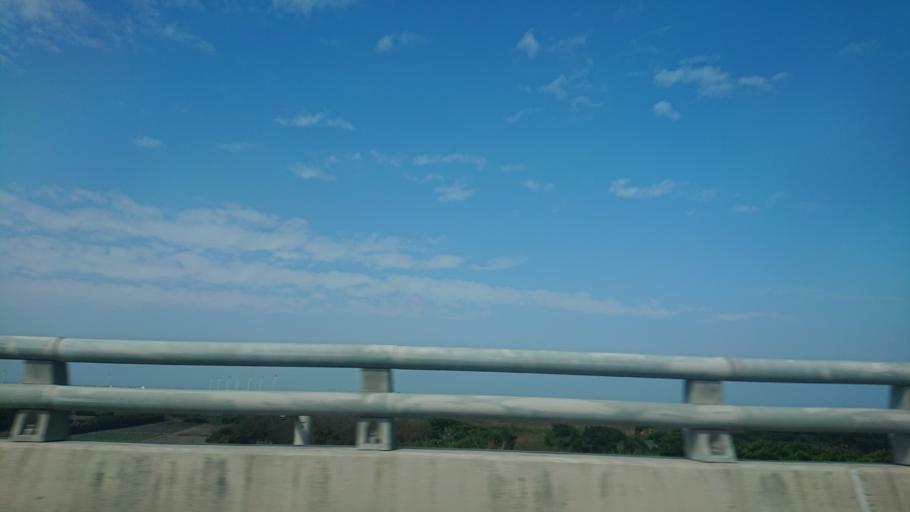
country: TW
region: Taiwan
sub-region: Changhua
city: Chang-hua
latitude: 23.9840
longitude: 120.3665
